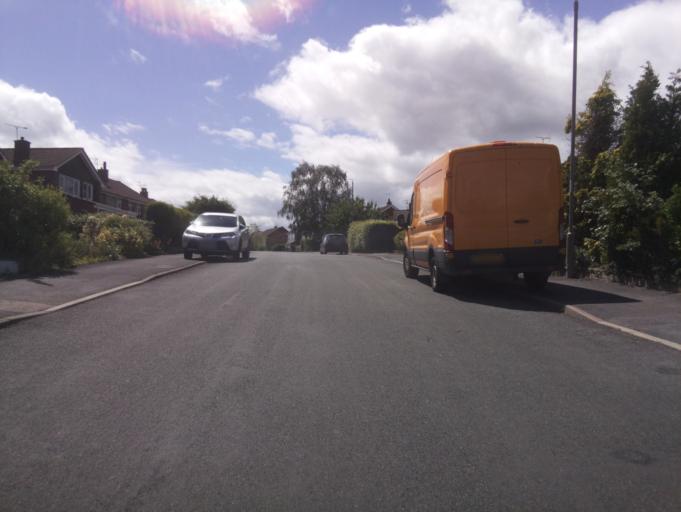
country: GB
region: England
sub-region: Nottinghamshire
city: Cotgrave
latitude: 52.8781
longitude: -1.0824
